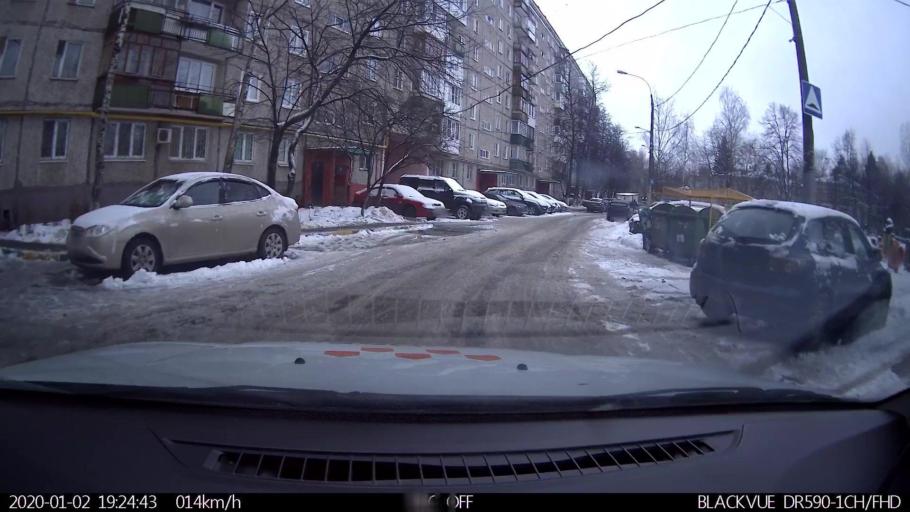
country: RU
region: Nizjnij Novgorod
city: Nizhniy Novgorod
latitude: 56.3202
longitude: 43.8744
